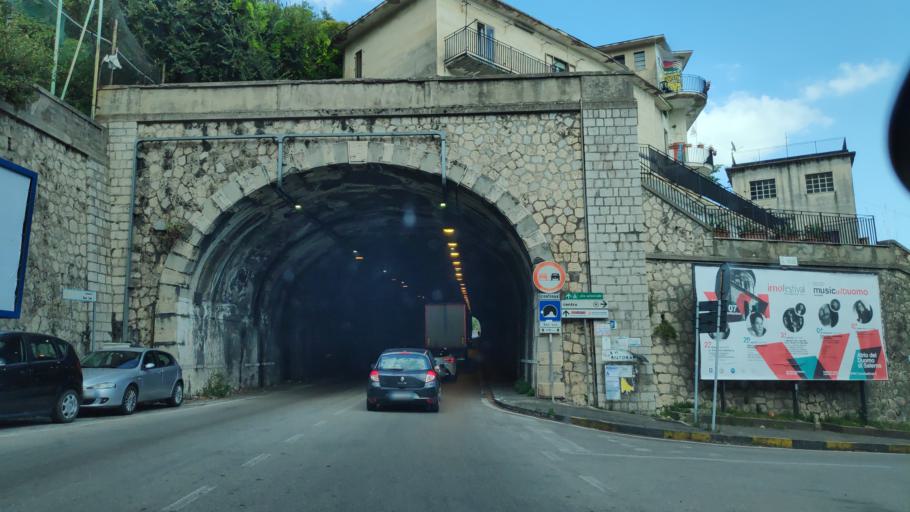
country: IT
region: Campania
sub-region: Provincia di Salerno
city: Capezzano Inferiore
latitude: 40.6823
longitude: 14.7520
